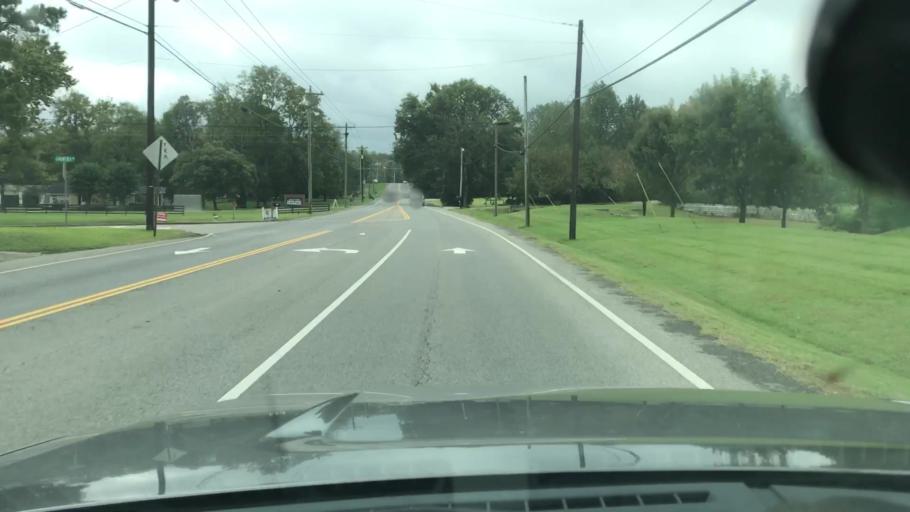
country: US
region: Tennessee
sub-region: Williamson County
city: Franklin
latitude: 35.9671
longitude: -86.8380
